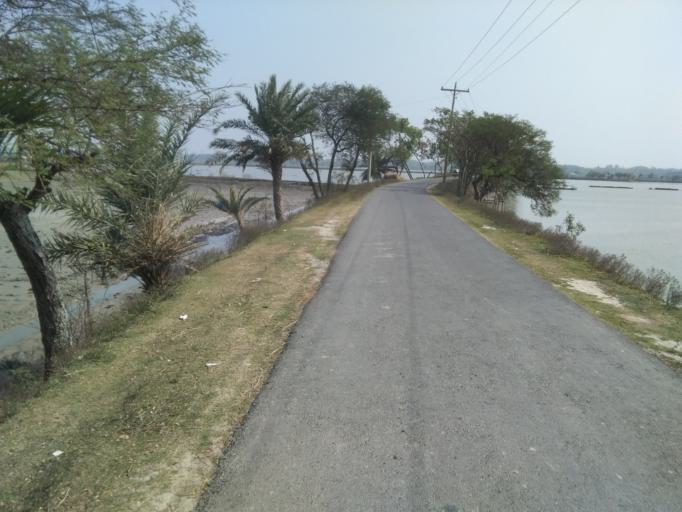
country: IN
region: West Bengal
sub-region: North 24 Parganas
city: Taki
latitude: 22.5939
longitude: 88.9826
